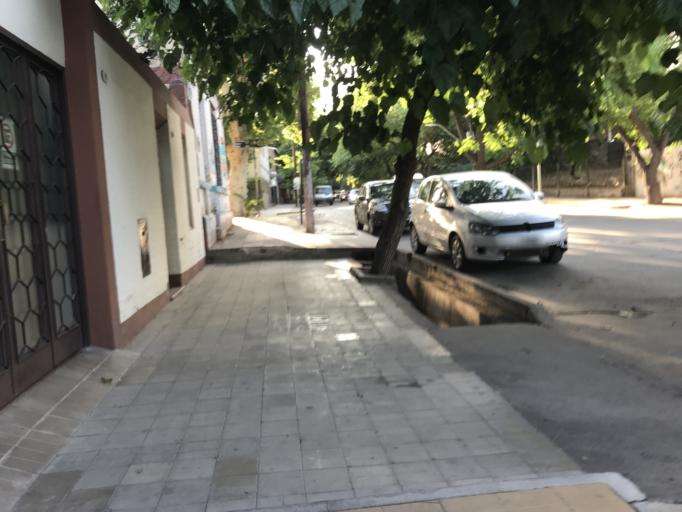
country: AR
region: Mendoza
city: Mendoza
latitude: -32.8799
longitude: -68.8401
